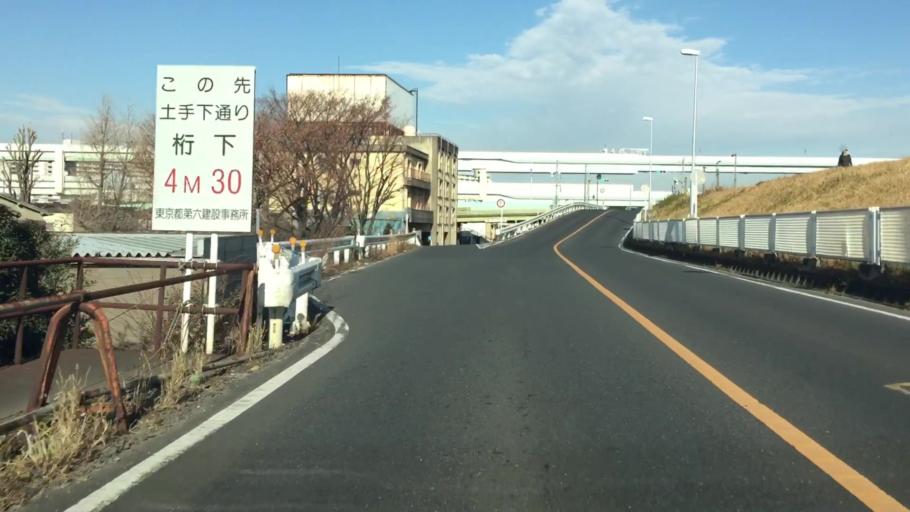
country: JP
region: Saitama
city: Kawaguchi
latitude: 35.7614
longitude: 139.7591
